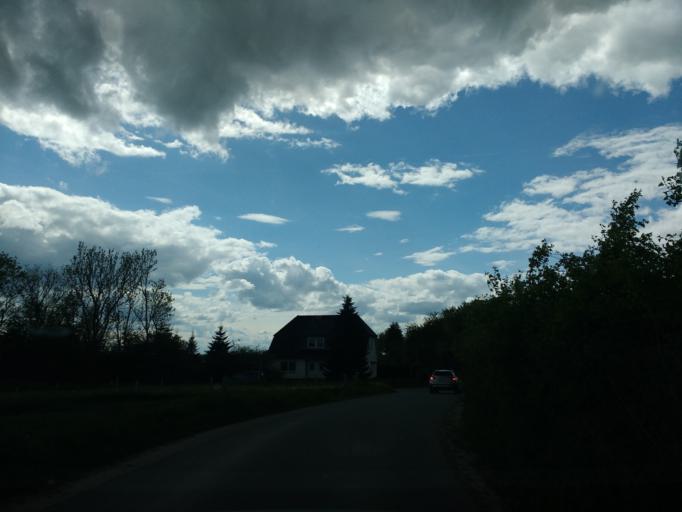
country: DE
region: Schleswig-Holstein
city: Barkelsby
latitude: 54.4955
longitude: 9.8614
